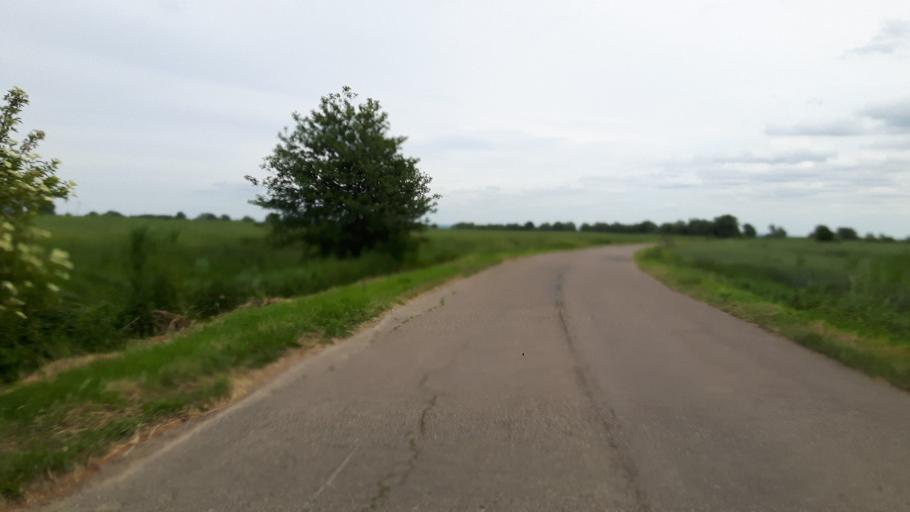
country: PL
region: Pomeranian Voivodeship
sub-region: Powiat nowodworski
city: Sztutowo
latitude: 54.2705
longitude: 19.2022
